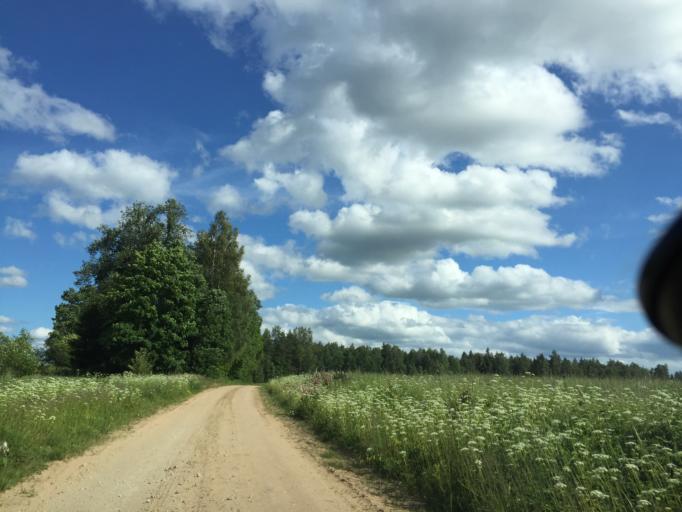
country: LV
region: Vecumnieki
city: Vecumnieki
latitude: 56.4235
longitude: 24.6051
